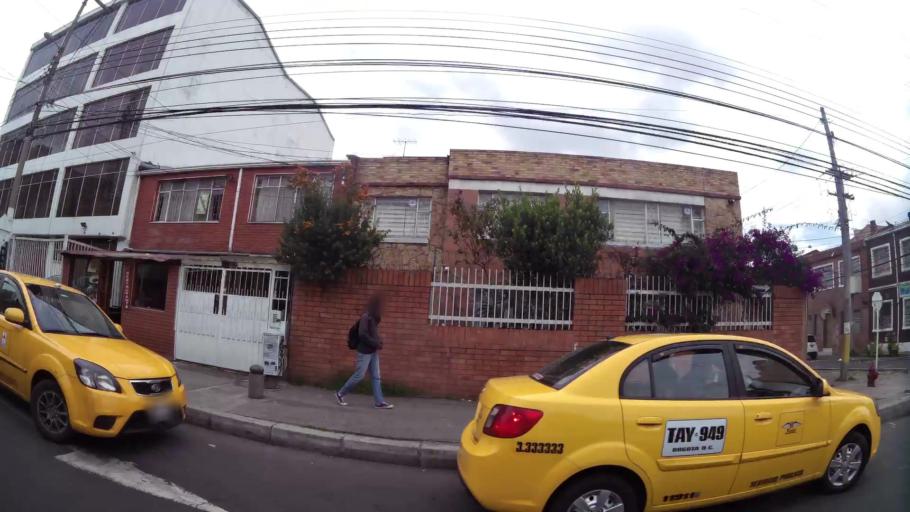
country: CO
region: Bogota D.C.
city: Bogota
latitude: 4.6304
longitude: -74.0875
